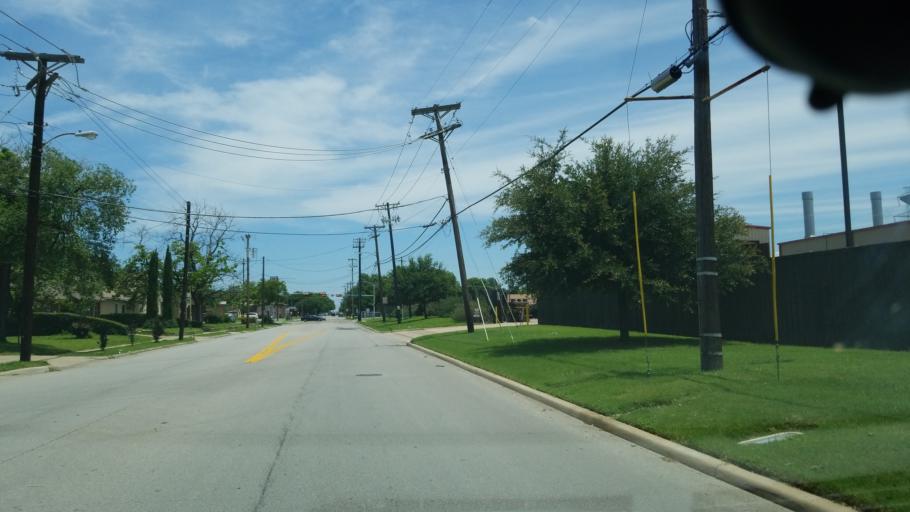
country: US
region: Texas
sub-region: Dallas County
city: Irving
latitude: 32.8176
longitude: -96.9361
